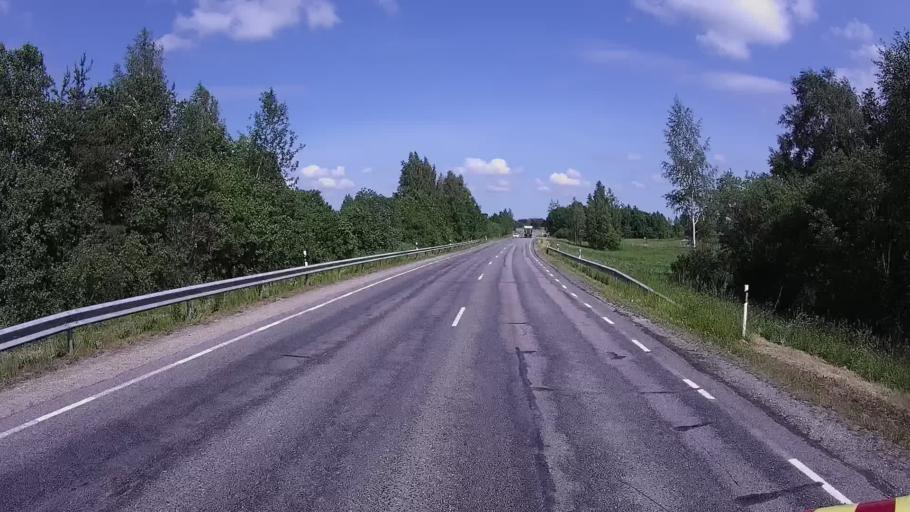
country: EE
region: Tartu
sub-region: UElenurme vald
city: Ulenurme
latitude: 58.2814
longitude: 26.7285
